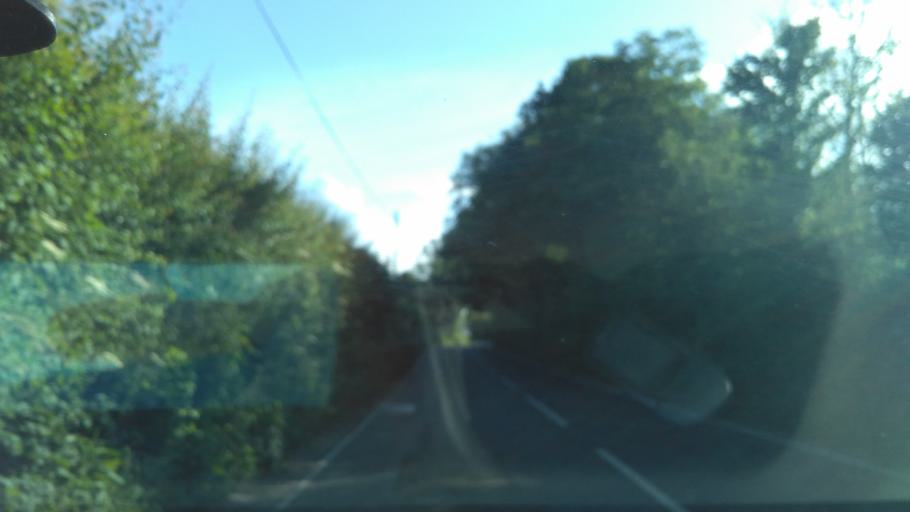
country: GB
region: England
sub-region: Kent
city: Faversham
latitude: 51.2625
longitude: 0.8792
